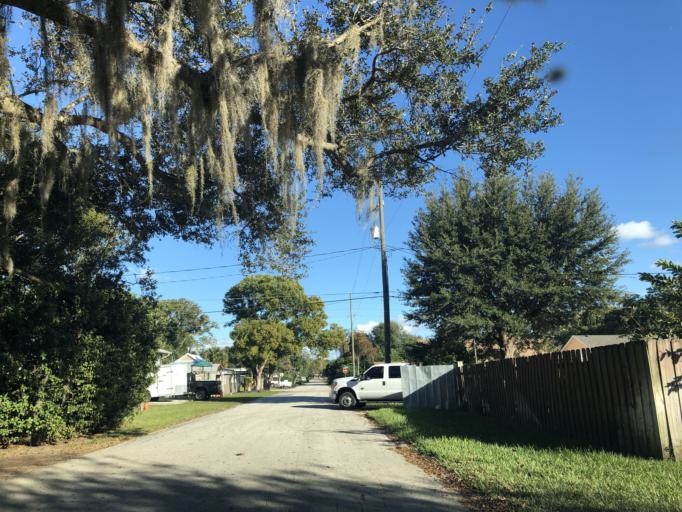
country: US
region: Florida
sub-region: Osceola County
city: Saint Cloud
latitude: 28.2506
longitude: -81.2724
